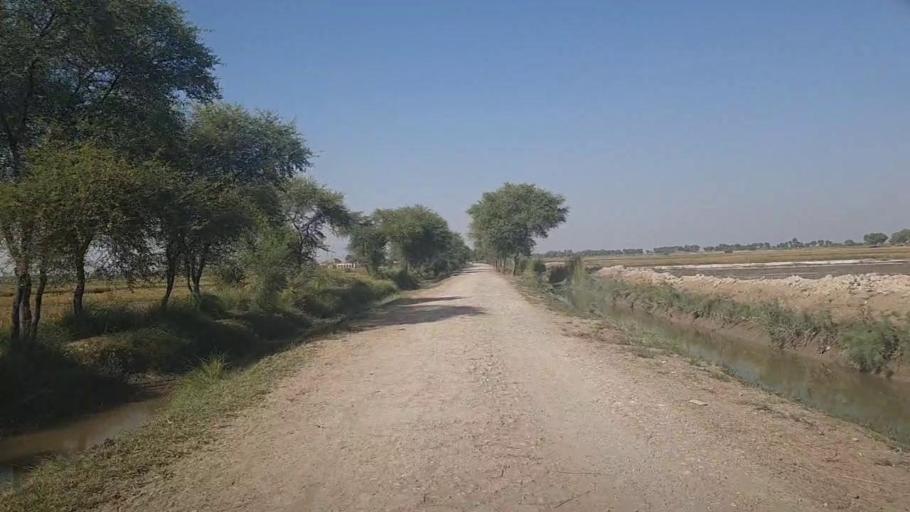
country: PK
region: Sindh
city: Thul
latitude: 28.3069
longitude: 68.7701
